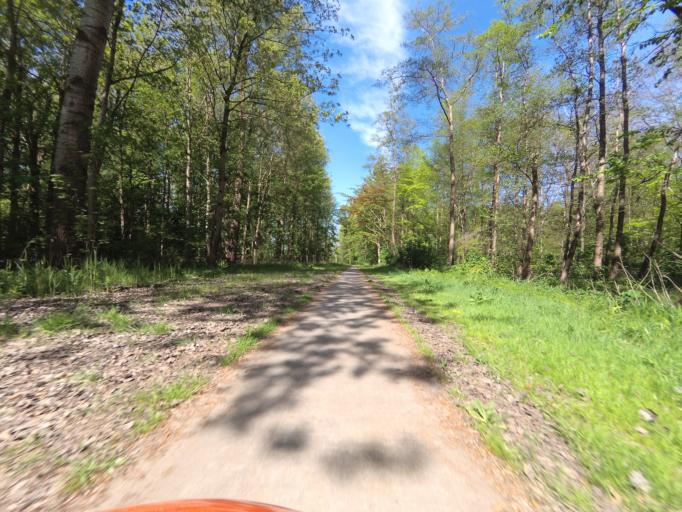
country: NL
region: Flevoland
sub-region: Gemeente Dronten
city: Dronten
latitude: 52.5179
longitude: 5.6420
